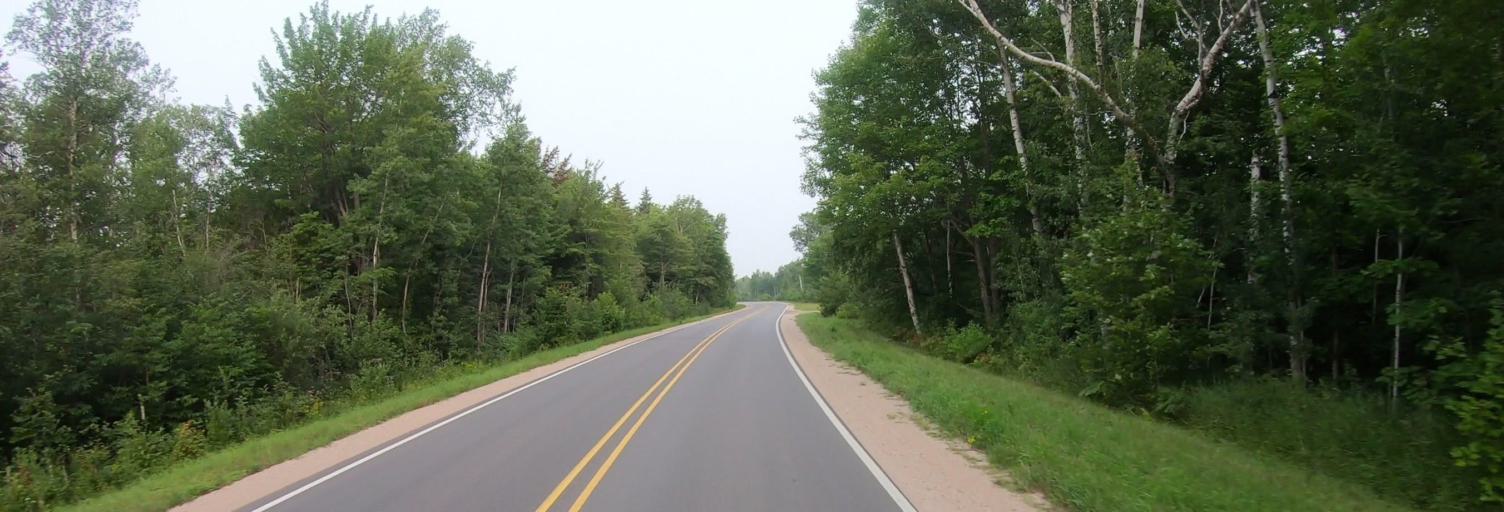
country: US
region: Michigan
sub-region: Chippewa County
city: Sault Ste. Marie
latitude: 46.4651
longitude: -84.9063
